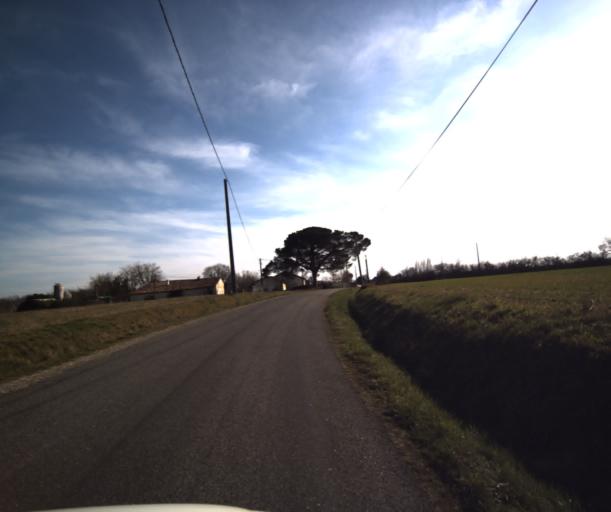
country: FR
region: Midi-Pyrenees
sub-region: Departement du Tarn-et-Garonne
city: Corbarieu
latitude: 43.9353
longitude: 1.3416
